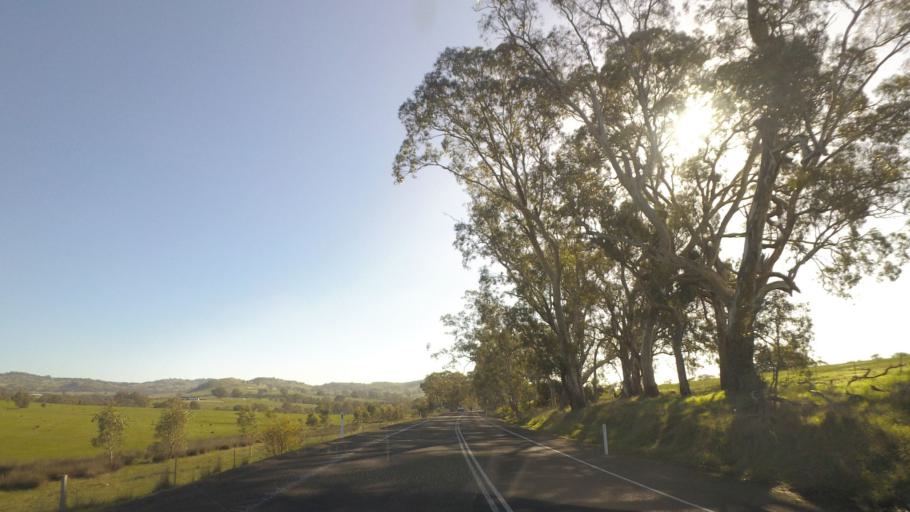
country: AU
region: Victoria
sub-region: Mount Alexander
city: Castlemaine
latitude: -36.9523
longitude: 144.3417
